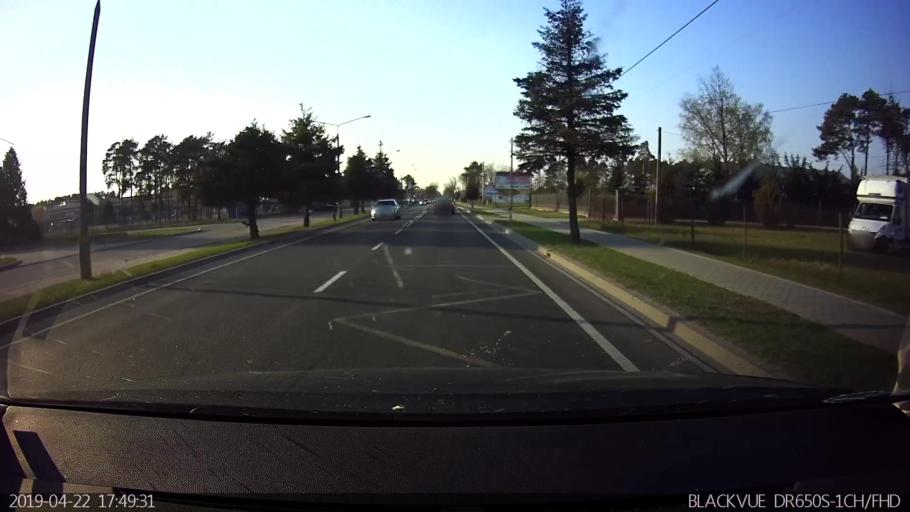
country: PL
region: Masovian Voivodeship
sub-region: Powiat wegrowski
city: Wegrow
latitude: 52.4148
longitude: 22.0082
